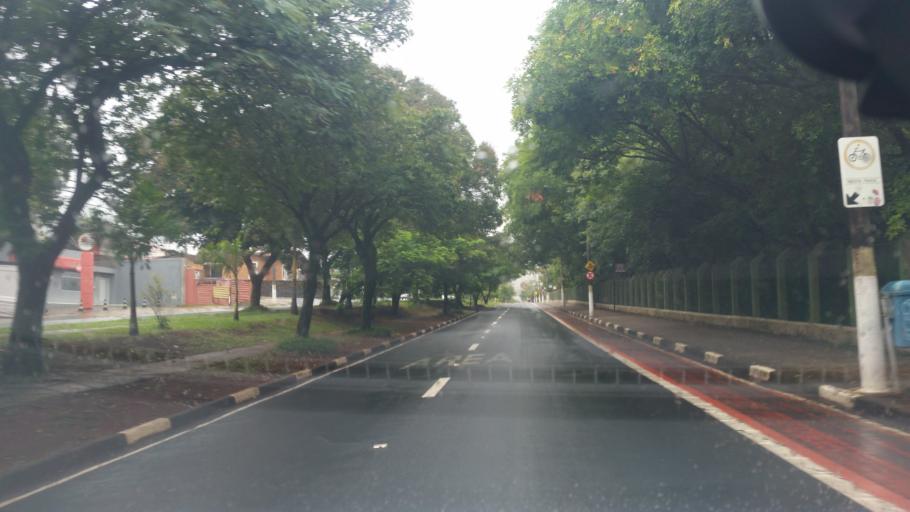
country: BR
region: Sao Paulo
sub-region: Campinas
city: Campinas
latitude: -22.8769
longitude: -47.0549
